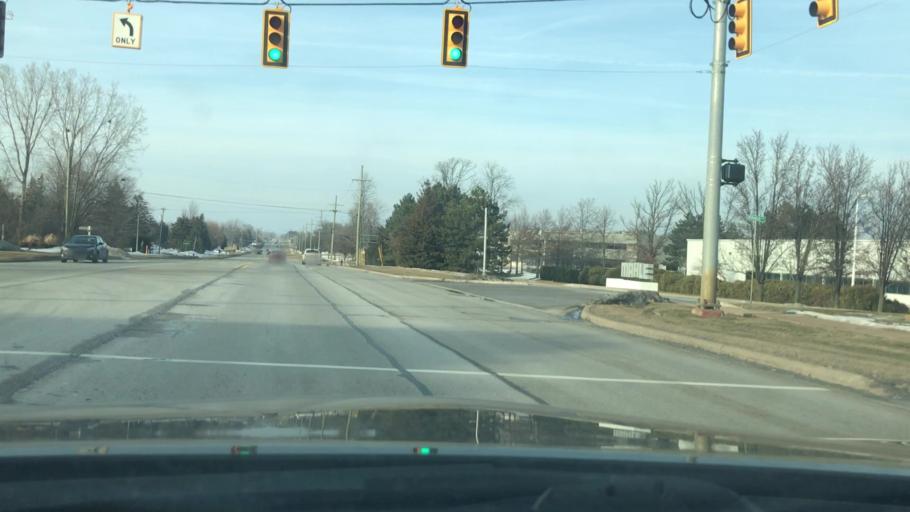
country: US
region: Michigan
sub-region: Oakland County
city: Novi
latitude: 42.4593
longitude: -83.4345
